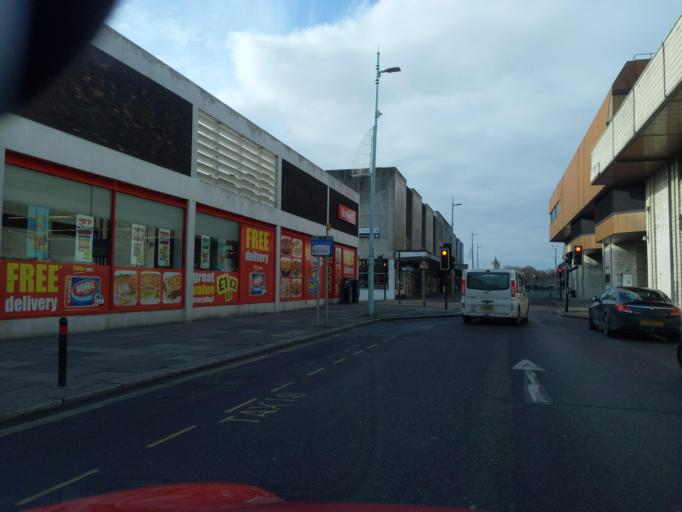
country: GB
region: England
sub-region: Plymouth
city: Plymouth
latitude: 50.3733
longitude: -4.1436
